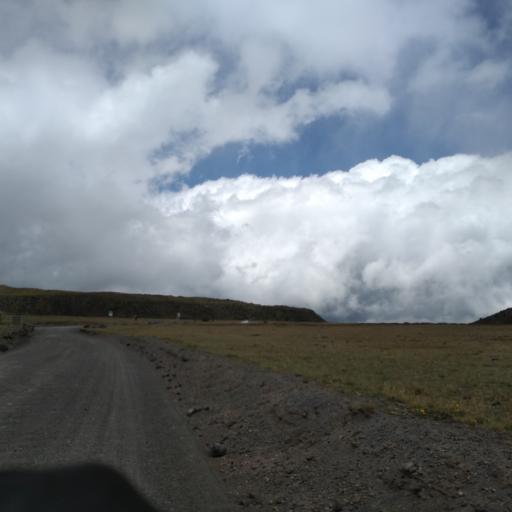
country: EC
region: Pichincha
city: Machachi
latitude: -0.6261
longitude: -78.4746
